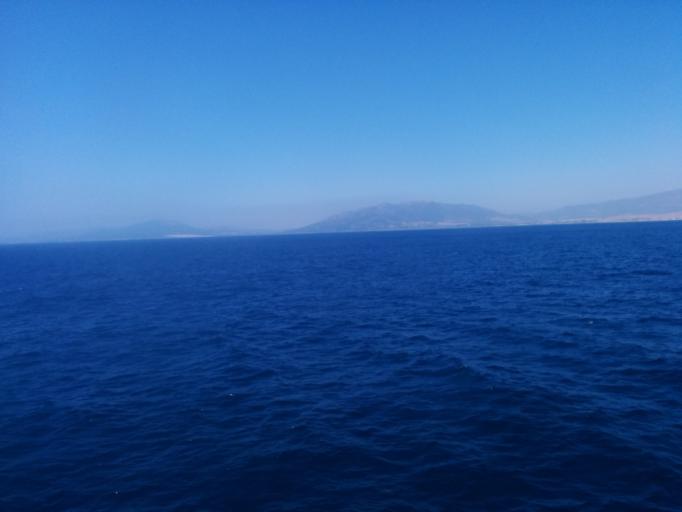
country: ES
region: Andalusia
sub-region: Provincia de Cadiz
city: Tarifa
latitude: 35.9924
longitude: -5.6195
